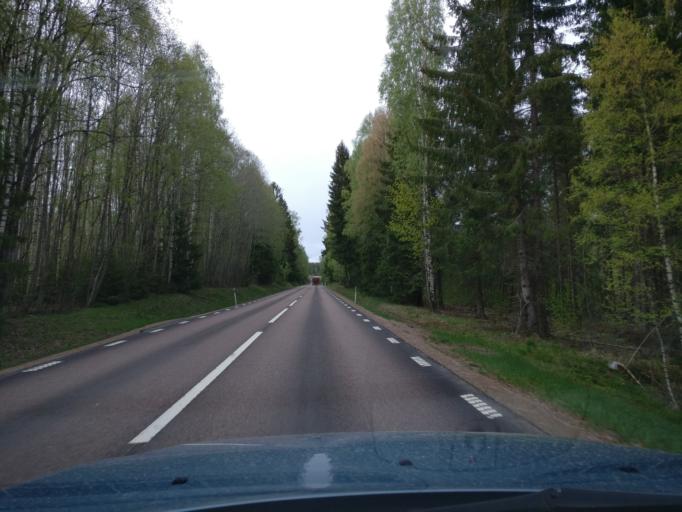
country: SE
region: Vaermland
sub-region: Forshaga Kommun
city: Deje
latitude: 59.6481
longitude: 13.4425
